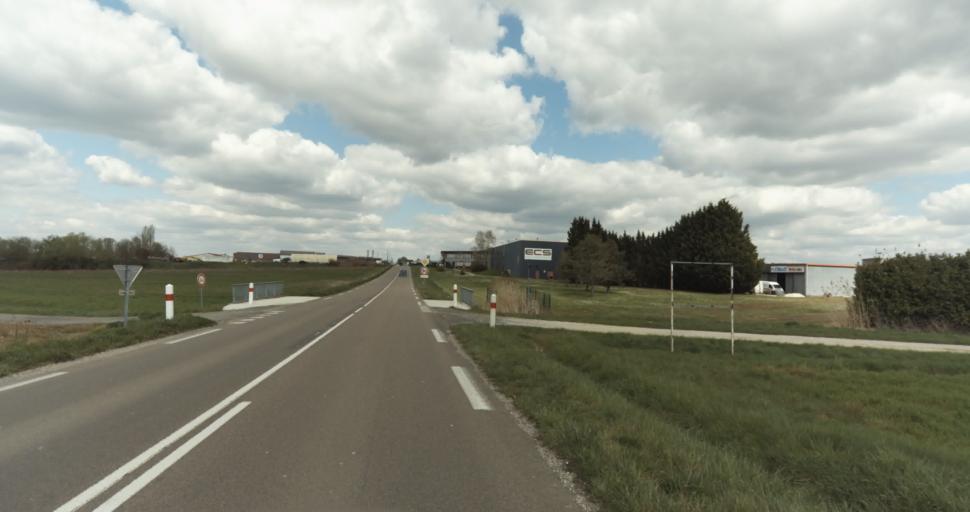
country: FR
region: Bourgogne
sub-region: Departement de la Cote-d'Or
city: Auxonne
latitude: 47.1754
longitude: 5.4018
